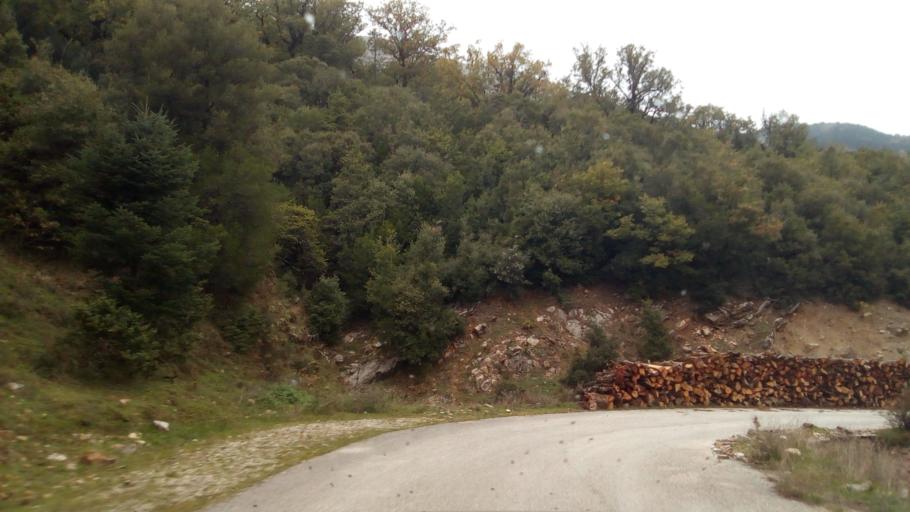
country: GR
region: West Greece
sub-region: Nomos Aitolias kai Akarnanias
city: Thermo
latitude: 38.6102
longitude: 21.8286
